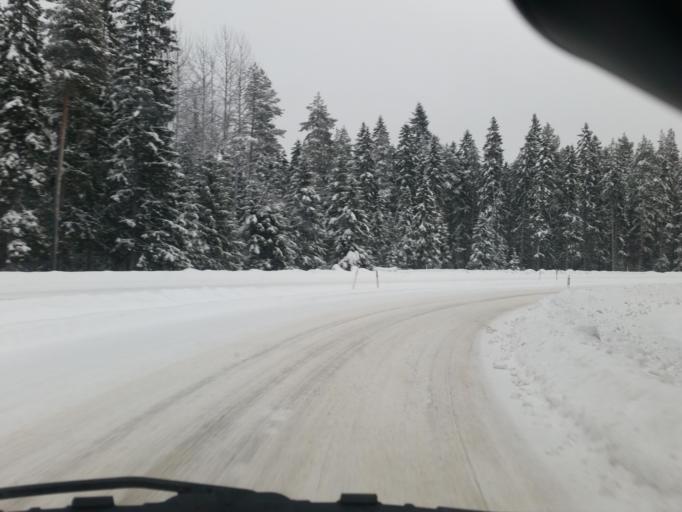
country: SE
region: Norrbotten
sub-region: Pitea Kommun
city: Norrfjarden
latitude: 65.3743
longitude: 21.4312
